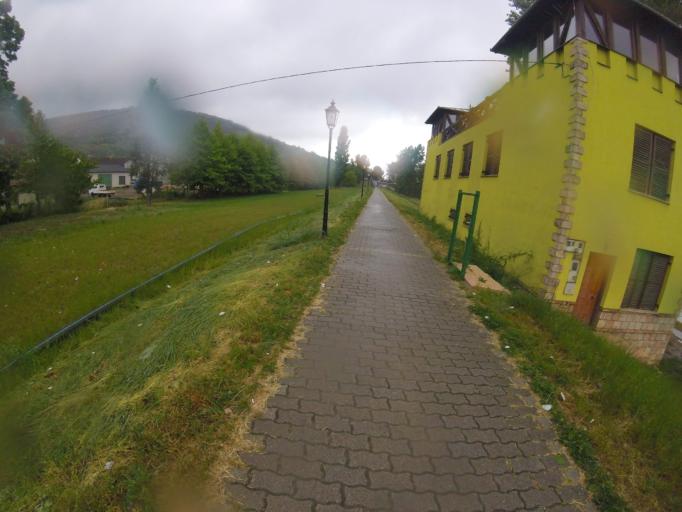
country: HU
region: Borsod-Abauj-Zemplen
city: Tokaj
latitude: 48.1146
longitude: 21.4152
